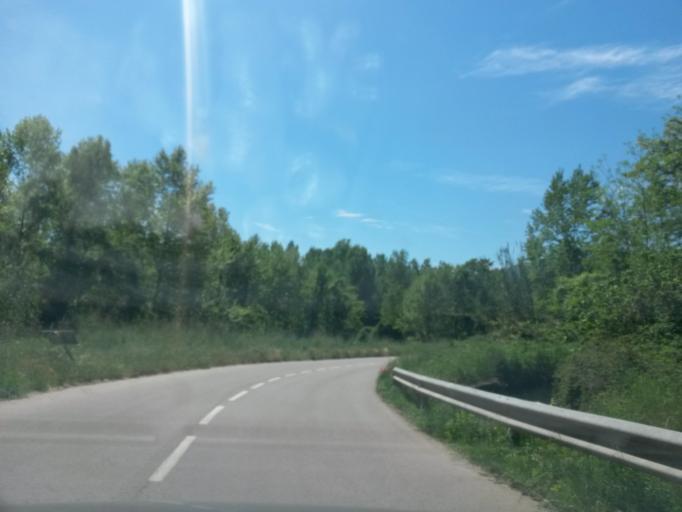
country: ES
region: Catalonia
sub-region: Provincia de Girona
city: Angles
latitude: 41.9664
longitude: 2.6653
